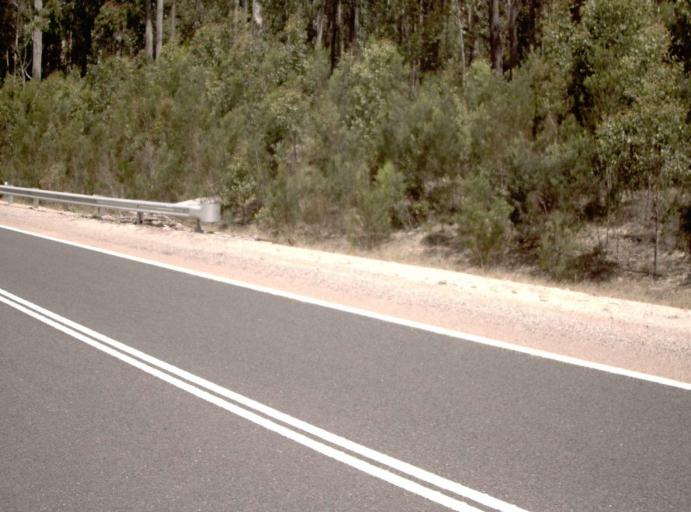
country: AU
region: New South Wales
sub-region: Bombala
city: Bombala
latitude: -37.5382
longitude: 149.4017
